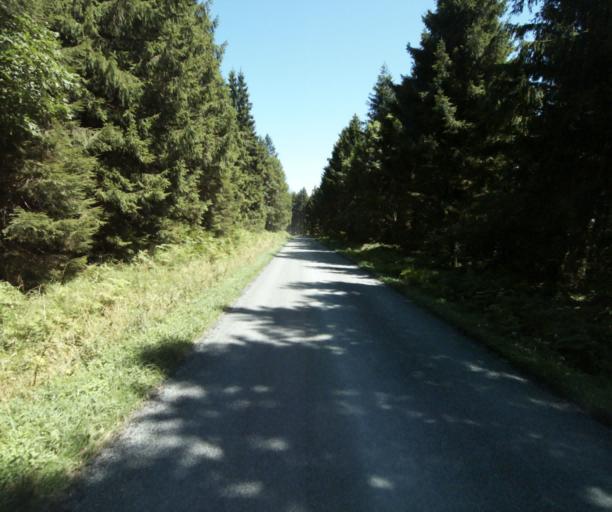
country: FR
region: Midi-Pyrenees
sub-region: Departement du Tarn
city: Dourgne
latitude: 43.4454
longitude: 2.1465
